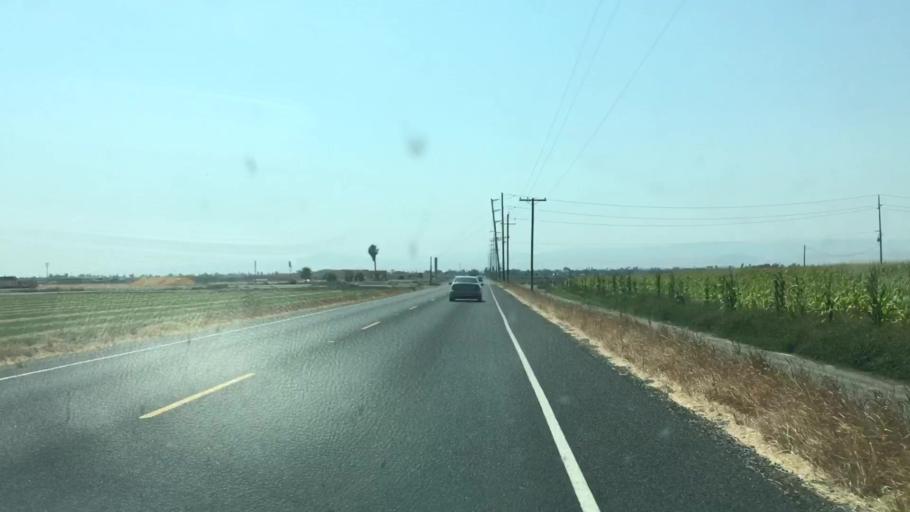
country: US
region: California
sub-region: San Joaquin County
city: Tracy
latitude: 37.7812
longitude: -121.4352
